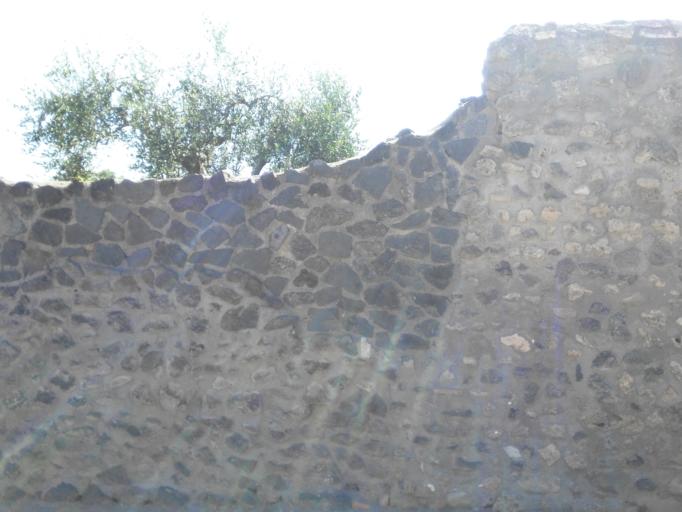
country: IT
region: Campania
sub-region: Provincia di Napoli
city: Pompei
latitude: 40.7503
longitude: 14.4918
